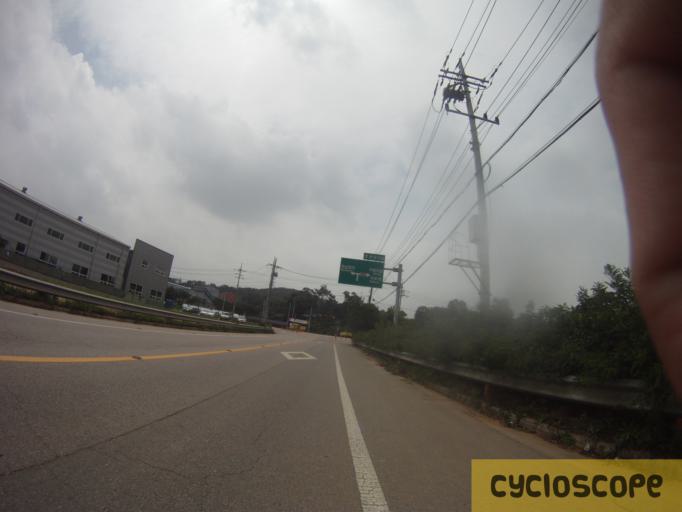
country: KR
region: Gyeonggi-do
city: Hwaseong-si
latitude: 37.1425
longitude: 126.8716
